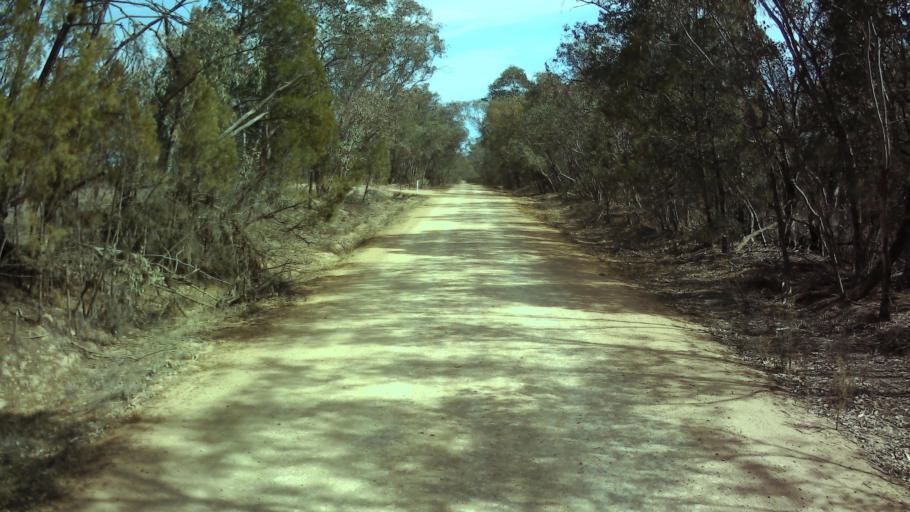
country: AU
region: New South Wales
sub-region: Weddin
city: Grenfell
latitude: -33.8769
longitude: 148.1494
